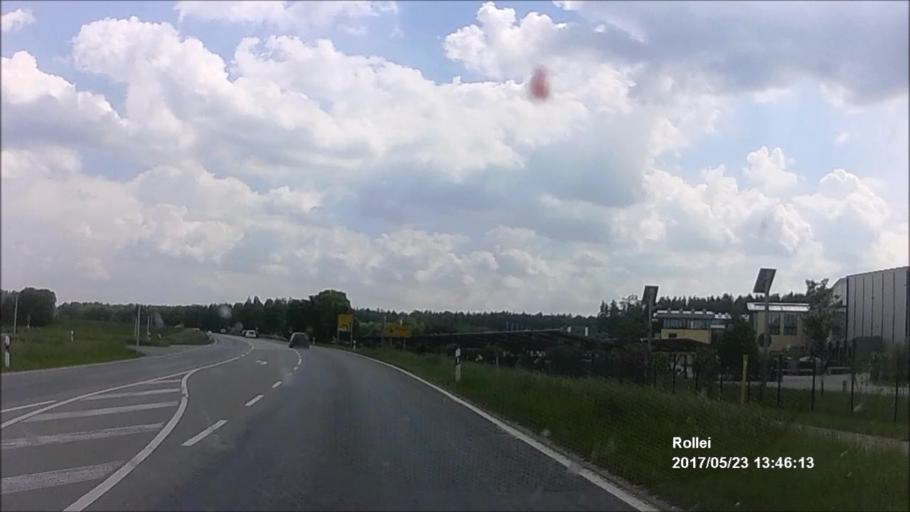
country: DE
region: Bavaria
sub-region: Upper Bavaria
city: Haag in Oberbayern
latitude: 48.1696
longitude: 12.1622
